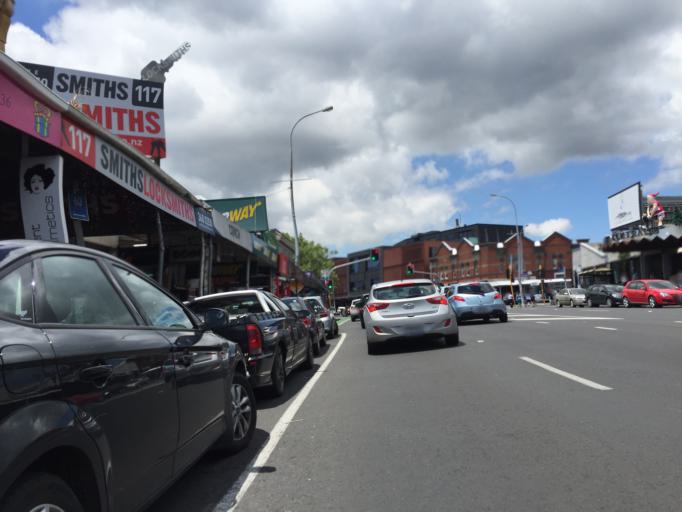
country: NZ
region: Auckland
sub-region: Auckland
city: Auckland
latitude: -36.8557
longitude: 174.7465
